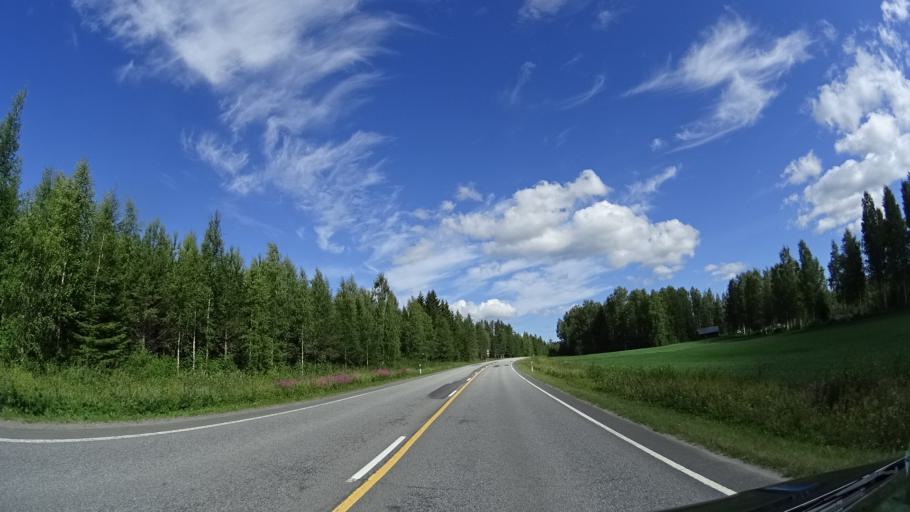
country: FI
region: Pirkanmaa
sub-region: Luoteis-Pirkanmaa
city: Kihnioe
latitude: 62.1638
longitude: 23.1624
